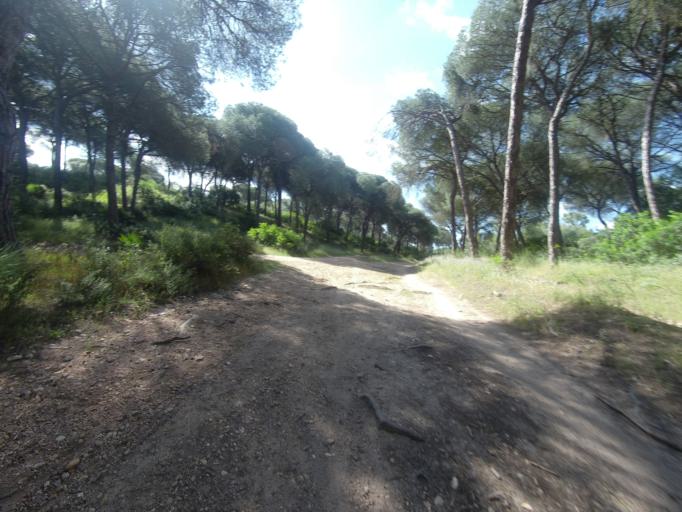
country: ES
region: Andalusia
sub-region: Provincia de Huelva
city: Aljaraque
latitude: 37.2376
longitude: -7.0304
